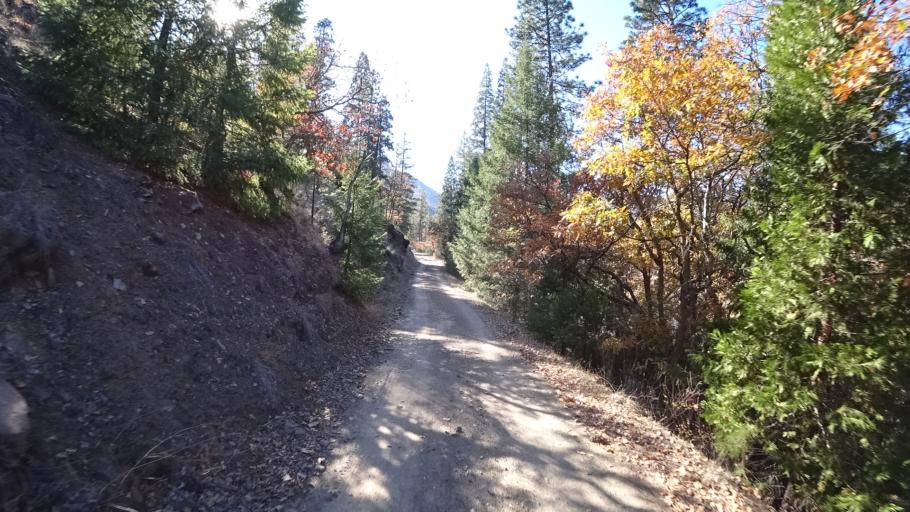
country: US
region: California
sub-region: Siskiyou County
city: Yreka
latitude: 41.8623
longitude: -122.7448
